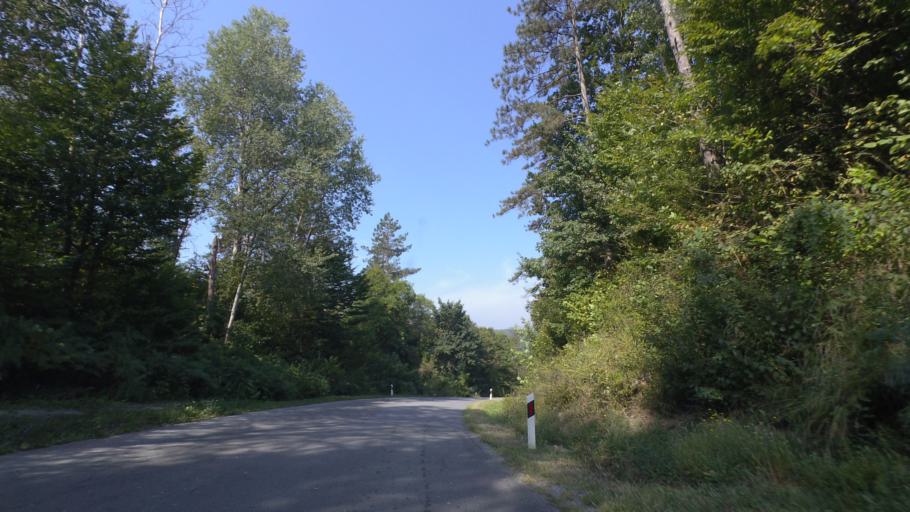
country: HR
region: Sisacko-Moslavacka
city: Dvor
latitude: 45.0786
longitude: 16.3251
